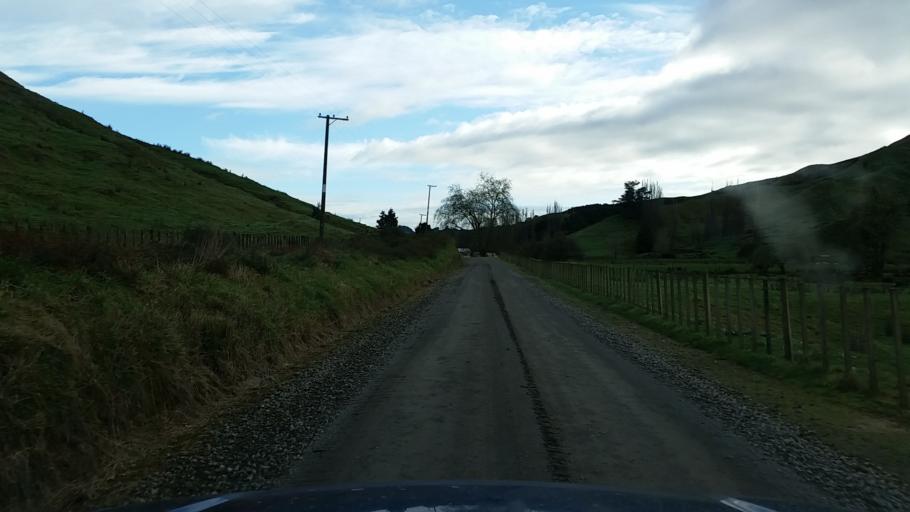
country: NZ
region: Taranaki
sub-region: New Plymouth District
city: Waitara
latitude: -39.0877
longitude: 174.8320
